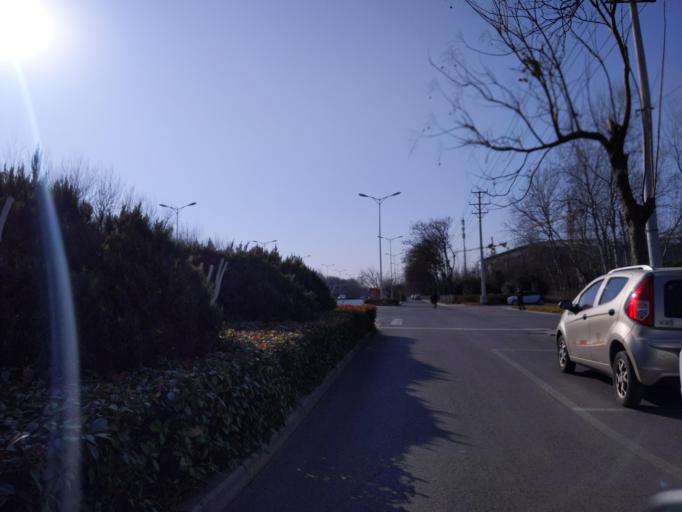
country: CN
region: Henan Sheng
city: Puyang
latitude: 35.7740
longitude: 114.9996
